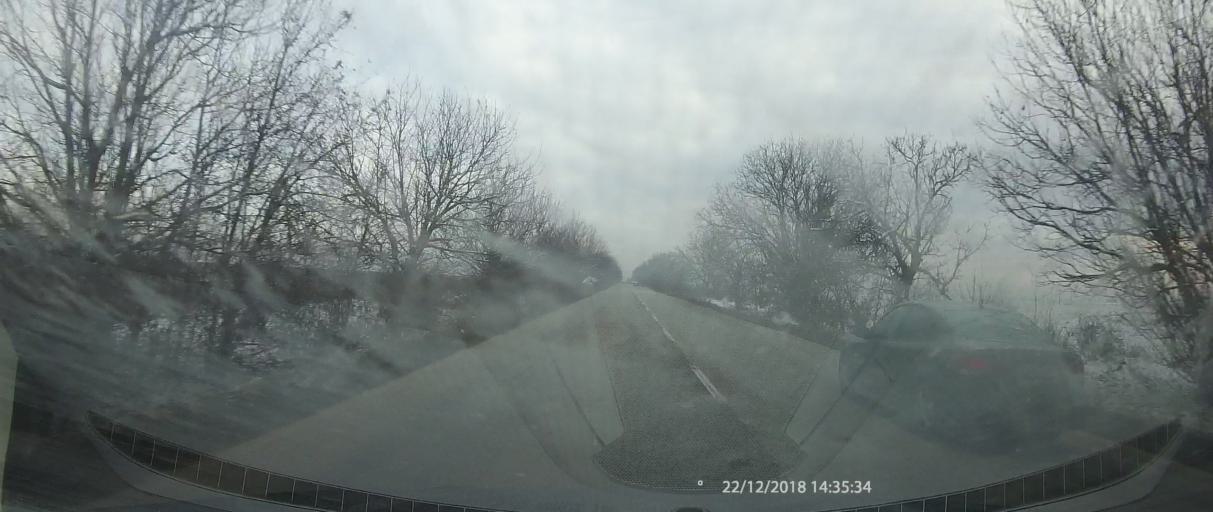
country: BG
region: Pleven
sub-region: Obshtina Levski
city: Levski
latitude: 43.4329
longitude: 25.0966
